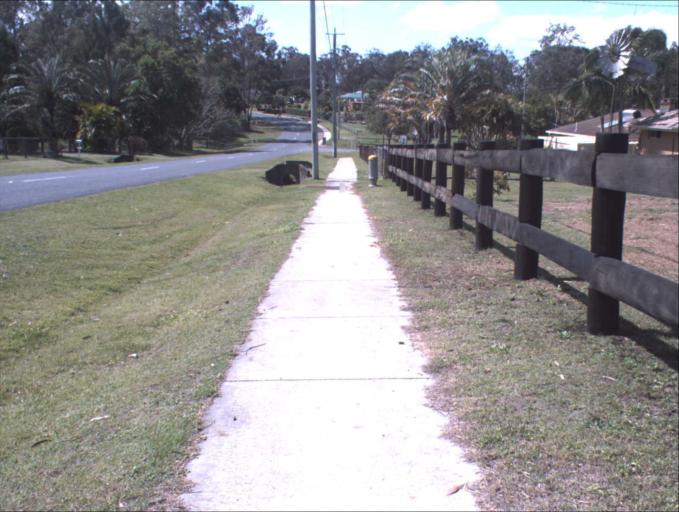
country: AU
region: Queensland
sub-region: Logan
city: Park Ridge South
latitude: -27.7301
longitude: 153.0431
